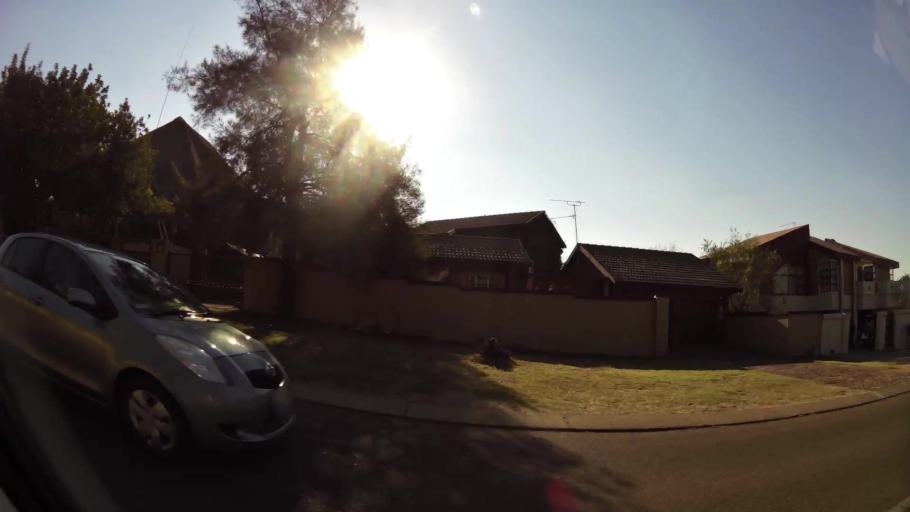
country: ZA
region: Gauteng
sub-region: City of Tshwane Metropolitan Municipality
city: Centurion
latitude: -25.8362
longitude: 28.2959
